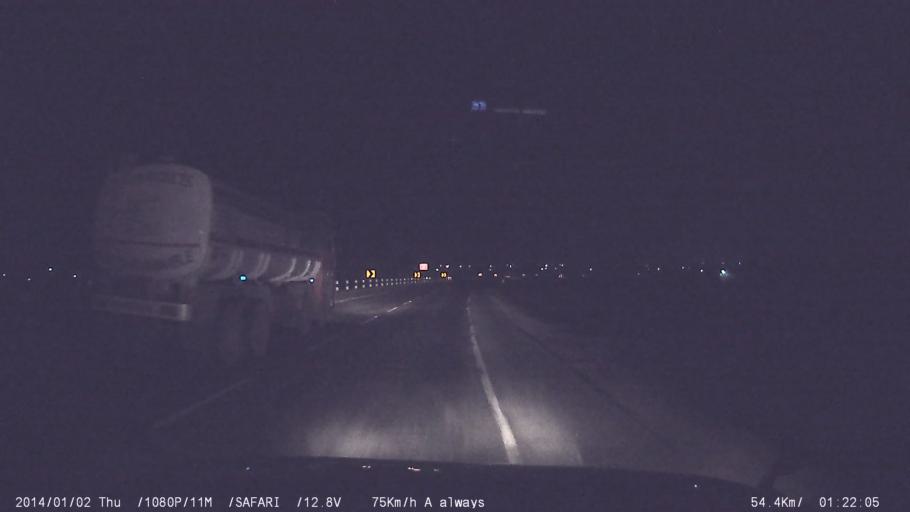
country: IN
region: Tamil Nadu
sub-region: Coimbatore
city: Irugur
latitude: 11.0496
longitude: 77.0788
